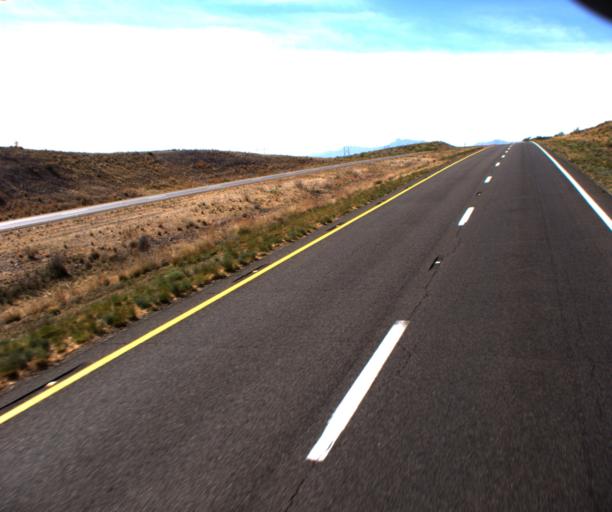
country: US
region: Arizona
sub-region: Graham County
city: Swift Trail Junction
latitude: 32.5099
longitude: -109.6742
